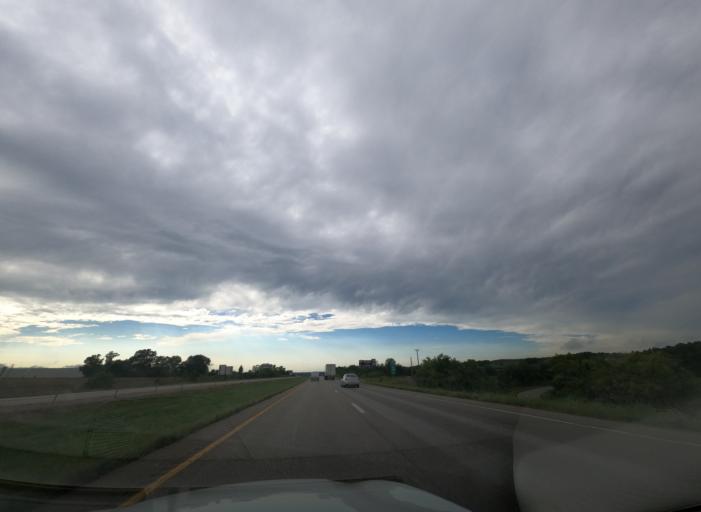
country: US
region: Missouri
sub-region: Sainte Genevieve County
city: Sainte Genevieve
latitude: 37.9391
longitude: -90.1267
